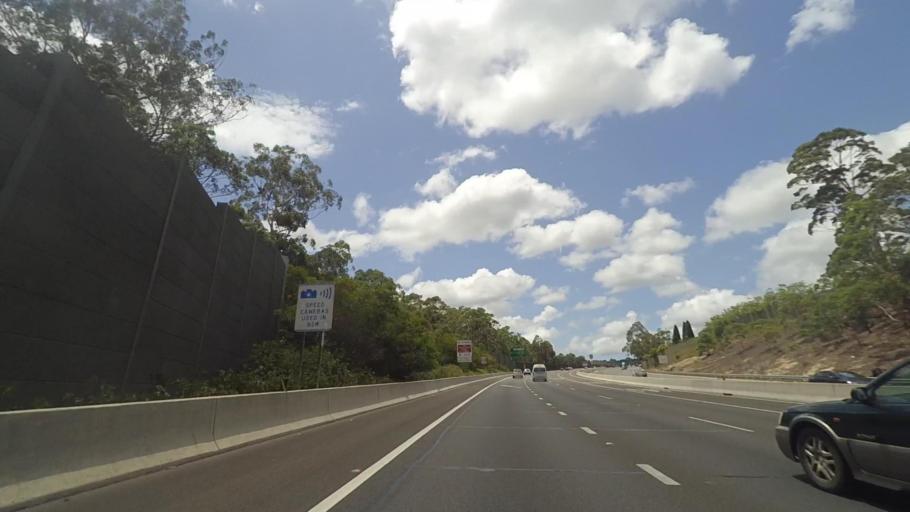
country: AU
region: New South Wales
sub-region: The Hills Shire
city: West Pennant
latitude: -33.7617
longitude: 151.0352
